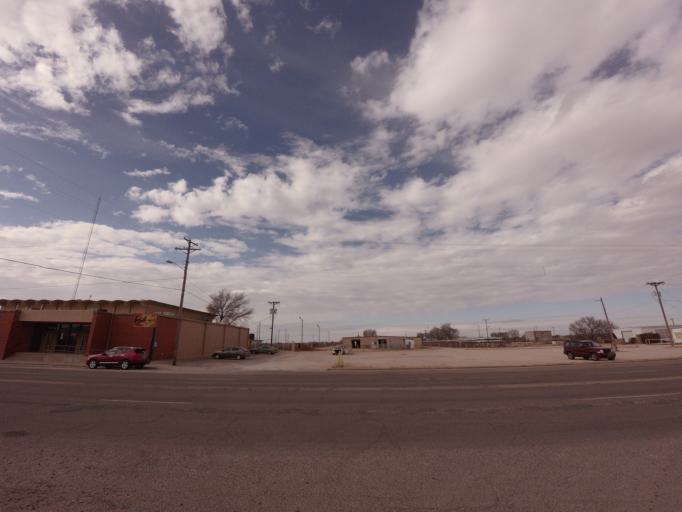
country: US
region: New Mexico
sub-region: Curry County
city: Clovis
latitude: 34.3939
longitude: -103.2203
